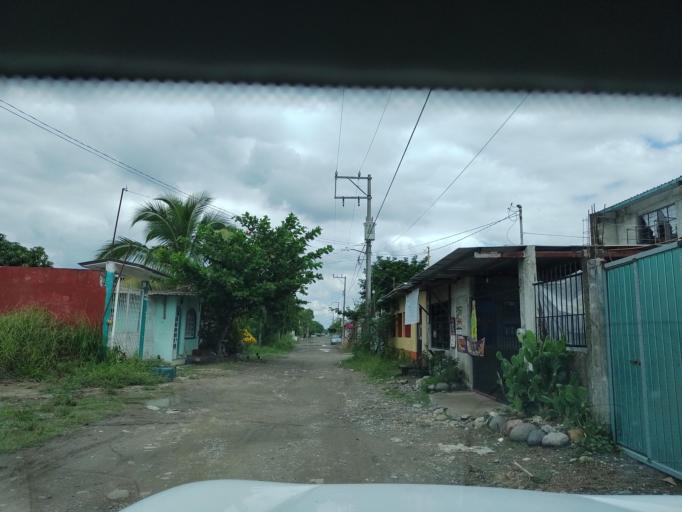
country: MX
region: Veracruz
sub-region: Atzalan
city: Colonias Pedernales
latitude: 20.0518
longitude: -97.0417
